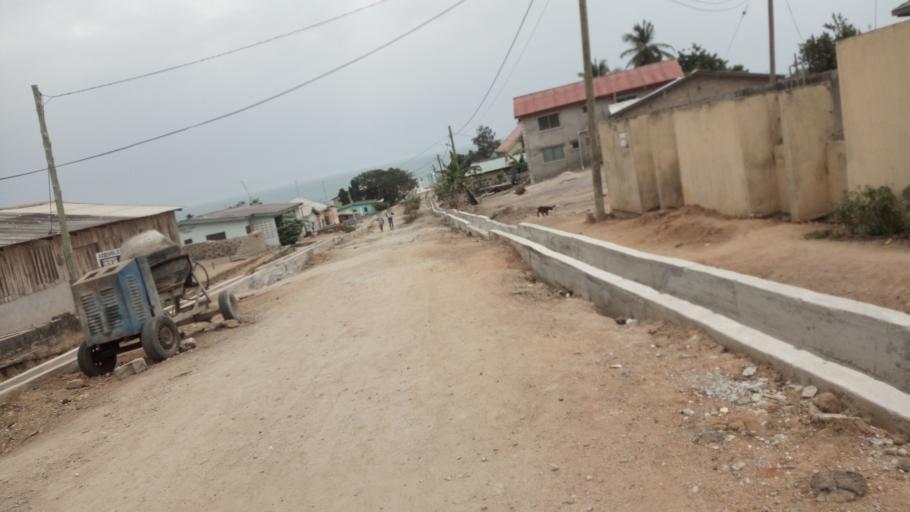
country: GH
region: Central
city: Winneba
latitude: 5.3357
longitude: -0.6225
